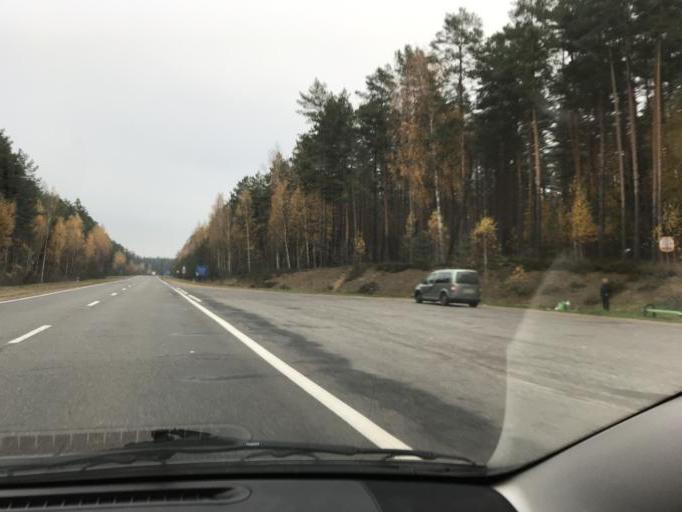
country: BY
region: Vitebsk
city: Syanno
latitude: 55.0578
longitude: 29.5242
